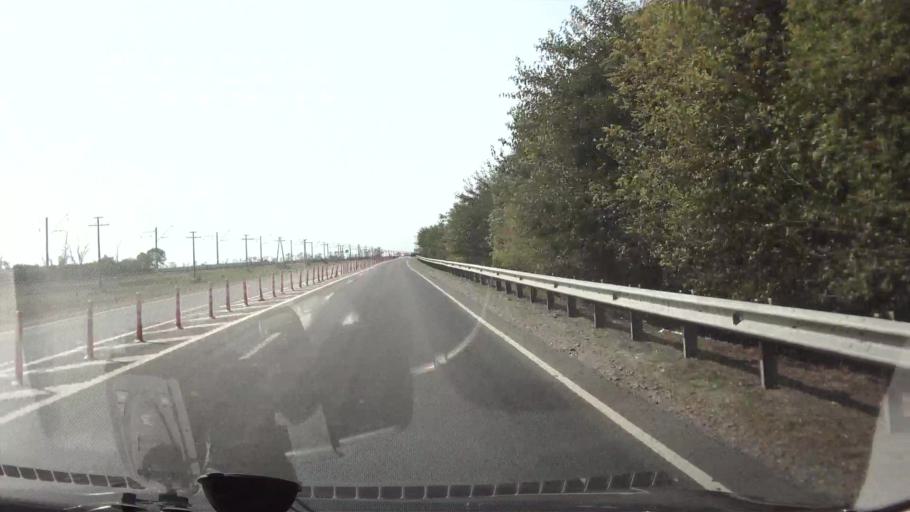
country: RU
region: Krasnodarskiy
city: Ladozhskaya
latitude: 45.2937
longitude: 39.8742
